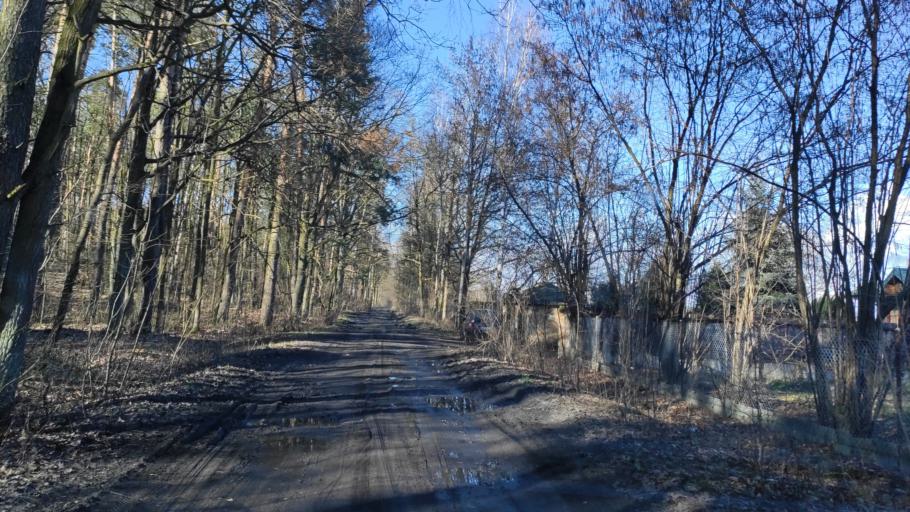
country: PL
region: Masovian Voivodeship
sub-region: Powiat radomski
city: Jedlnia-Letnisko
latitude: 51.4520
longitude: 21.3257
